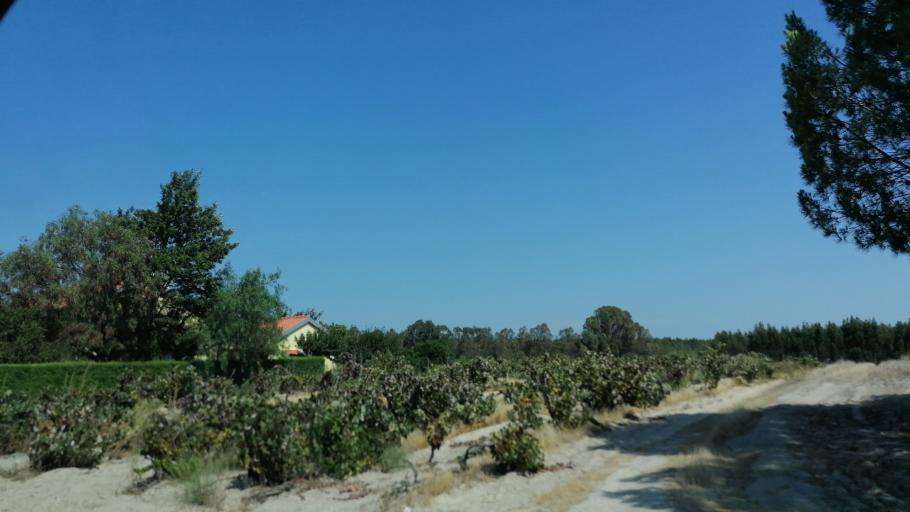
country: PT
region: Santarem
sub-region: Benavente
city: Poceirao
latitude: 38.7124
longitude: -8.7155
